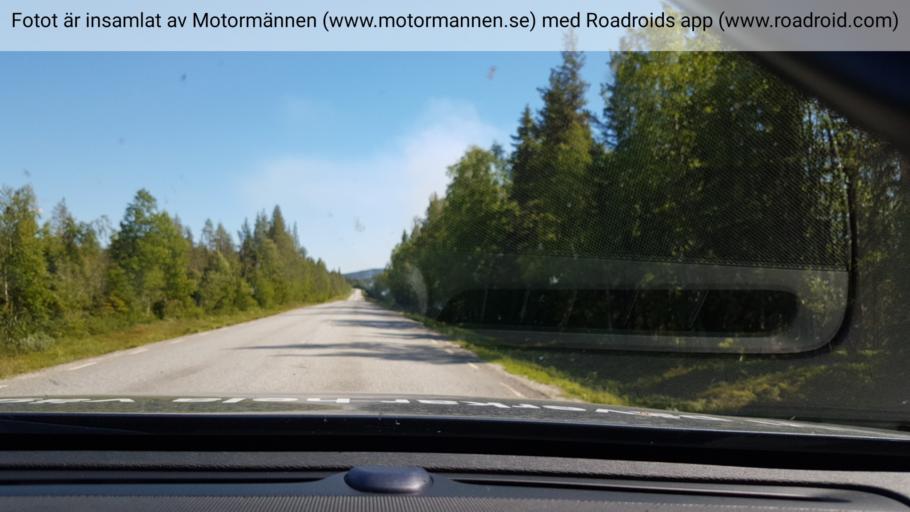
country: SE
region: Vaesterbotten
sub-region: Lycksele Kommun
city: Soderfors
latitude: 64.7042
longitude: 17.7238
